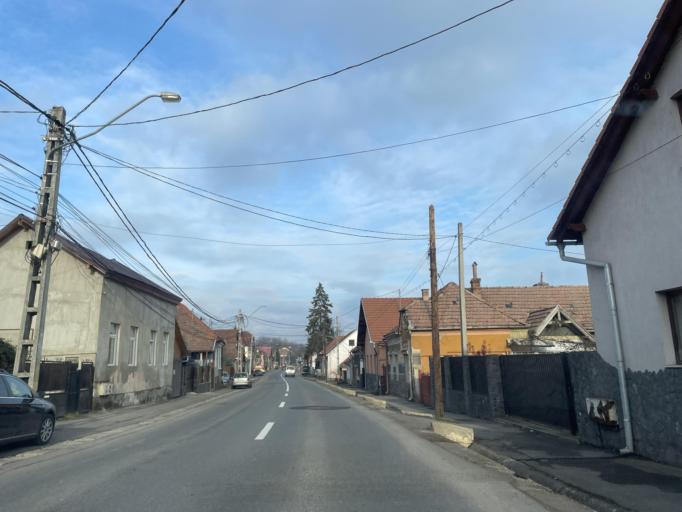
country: RO
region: Mures
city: Reghin-Sat
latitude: 46.7877
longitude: 24.7104
